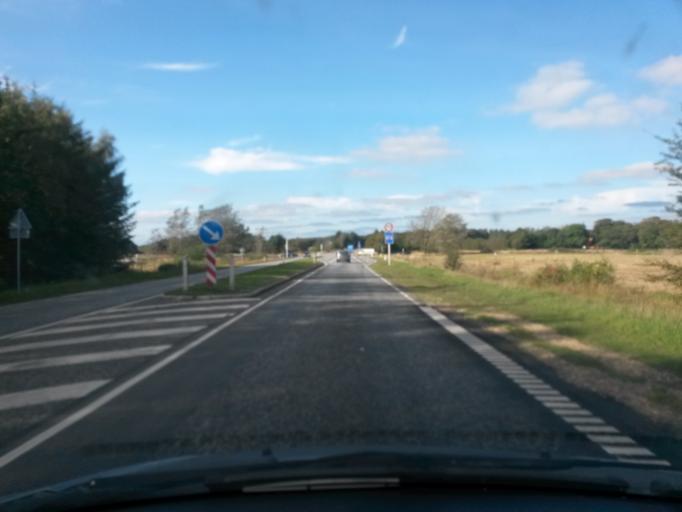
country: DK
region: Central Jutland
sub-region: Herning Kommune
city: Avlum
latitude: 56.2352
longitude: 8.8095
